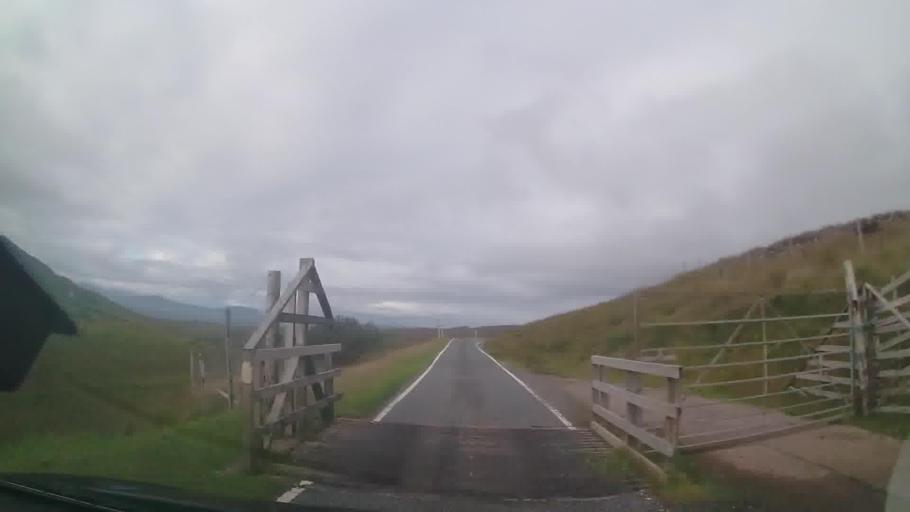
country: GB
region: Scotland
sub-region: Argyll and Bute
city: Isle Of Mull
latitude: 56.7269
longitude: -6.0371
